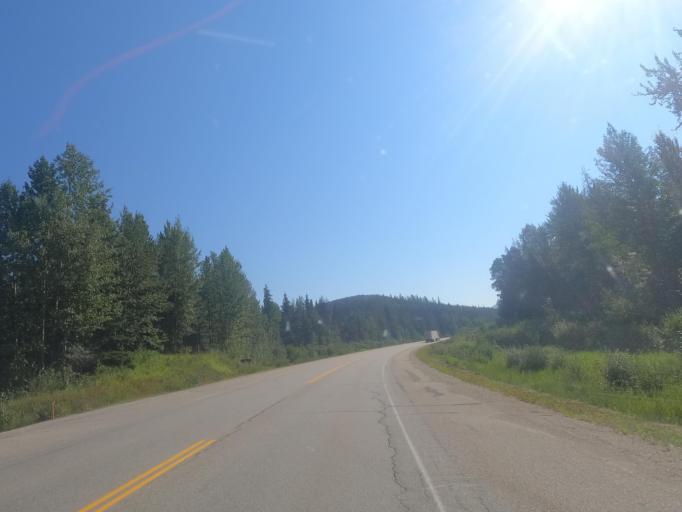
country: CA
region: Alberta
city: Jasper Park Lodge
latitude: 52.8881
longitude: -118.4758
